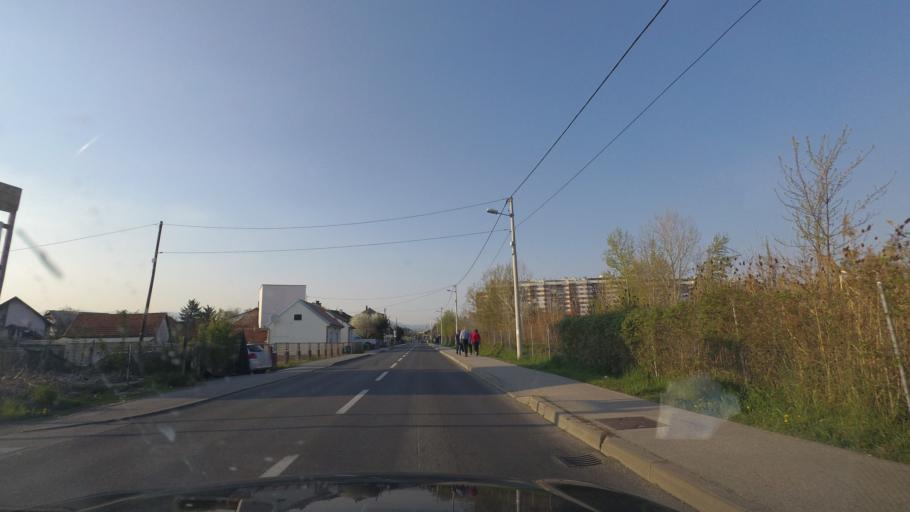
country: HR
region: Grad Zagreb
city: Dubrava
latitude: 45.8260
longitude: 16.0634
